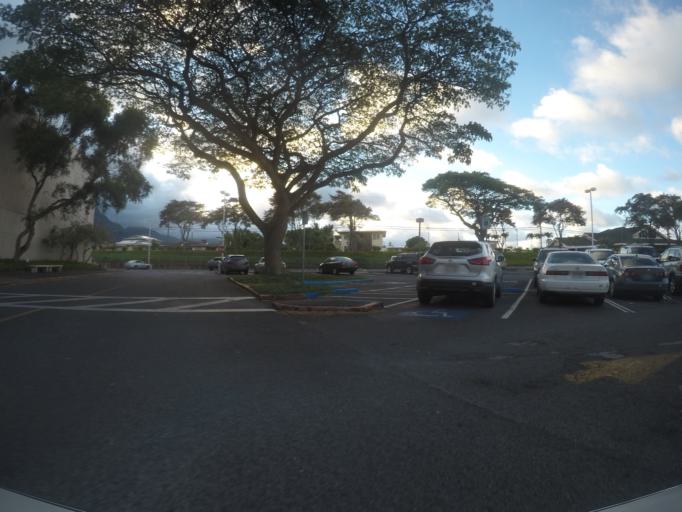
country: US
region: Hawaii
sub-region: Honolulu County
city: He'eia
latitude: 21.4207
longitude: -157.8057
